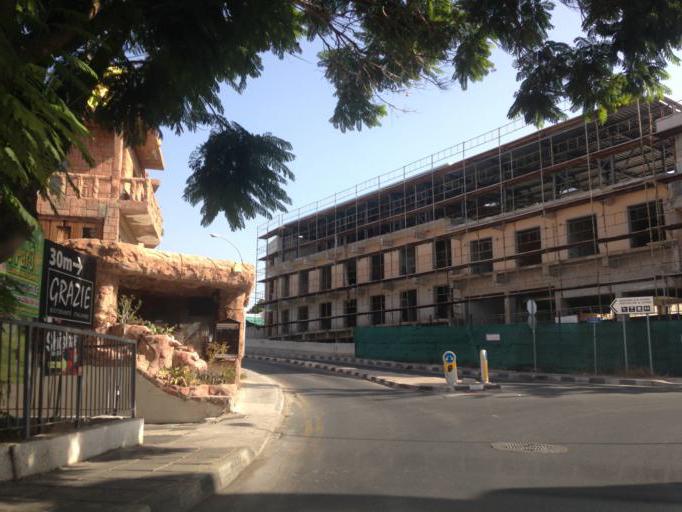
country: CY
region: Pafos
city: Paphos
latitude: 34.7566
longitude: 32.4147
